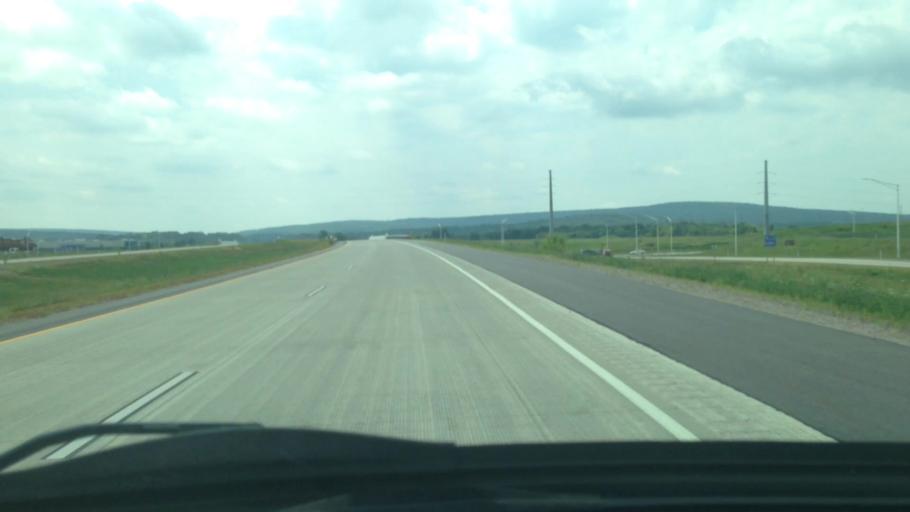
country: US
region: Wisconsin
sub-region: Sauk County
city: West Baraboo
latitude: 43.4625
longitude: -89.7779
